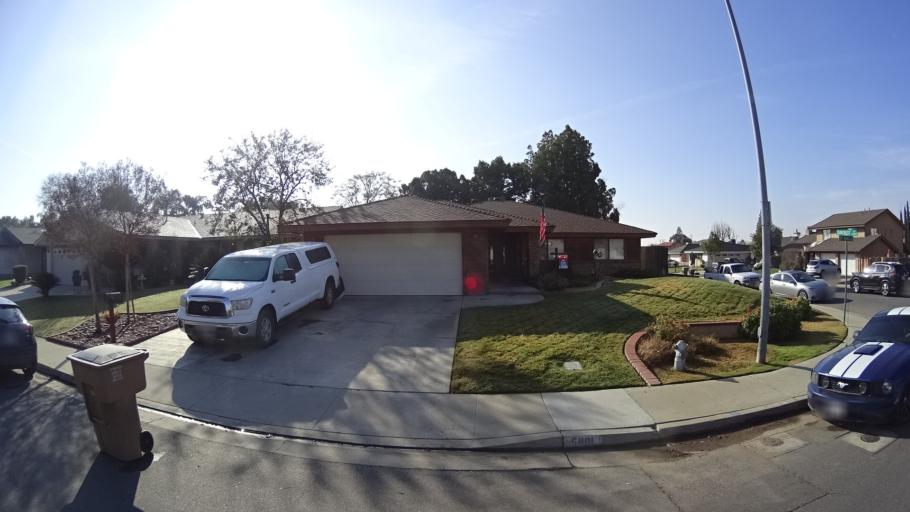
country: US
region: California
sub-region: Kern County
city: Oildale
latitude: 35.4045
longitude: -118.9287
